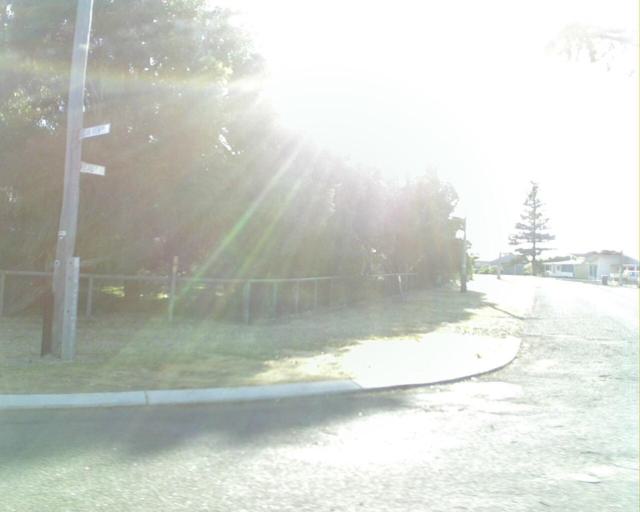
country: AU
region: Western Australia
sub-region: Dandaragan
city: Jurien Bay
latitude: -30.0643
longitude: 114.9665
